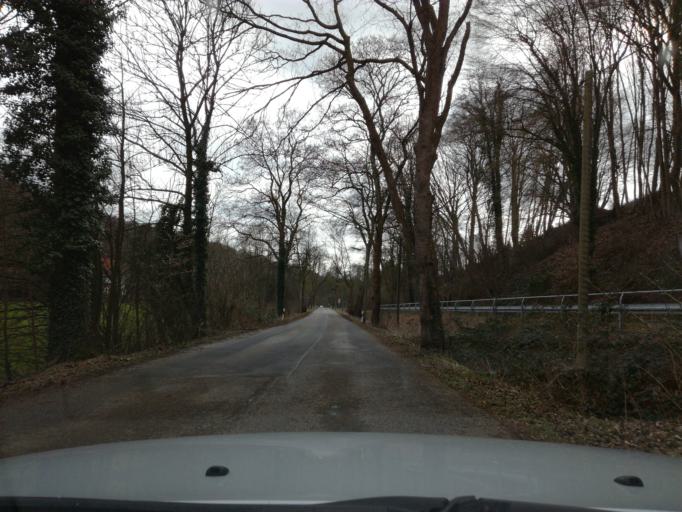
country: DE
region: North Rhine-Westphalia
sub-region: Regierungsbezirk Dusseldorf
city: Velbert
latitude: 51.3800
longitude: 7.0384
